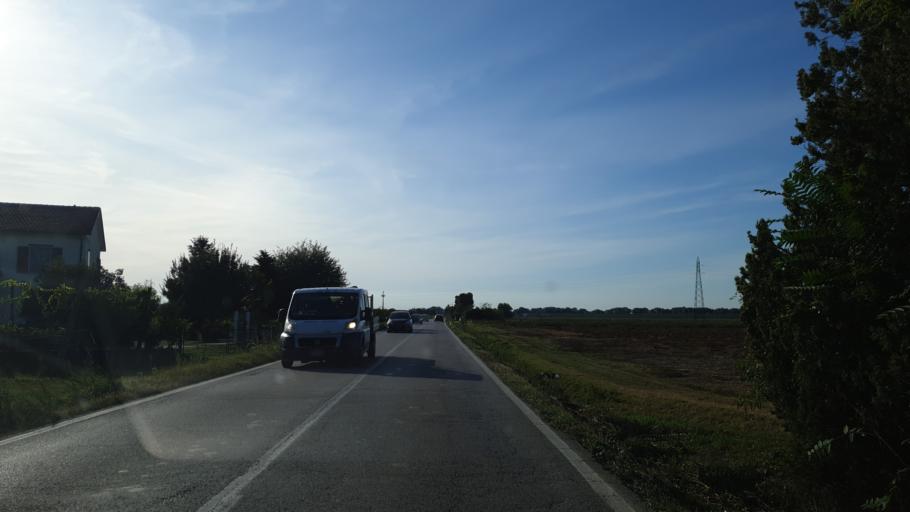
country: IT
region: Emilia-Romagna
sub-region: Provincia di Ravenna
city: Voltana
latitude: 44.5488
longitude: 11.9604
